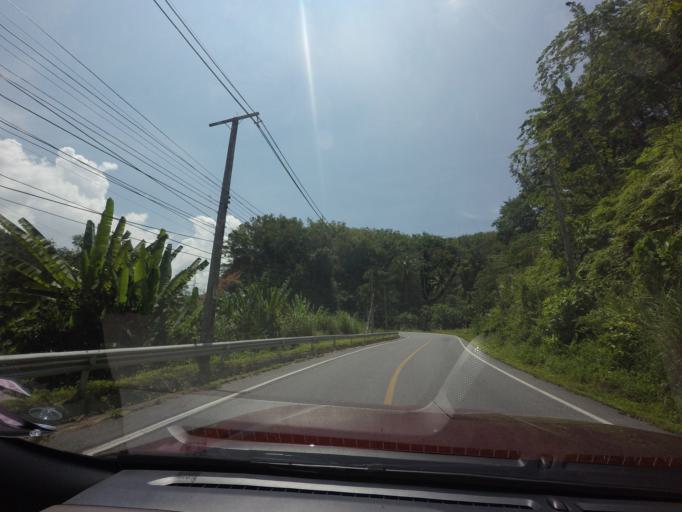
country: TH
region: Yala
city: Betong
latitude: 5.8966
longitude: 101.1464
